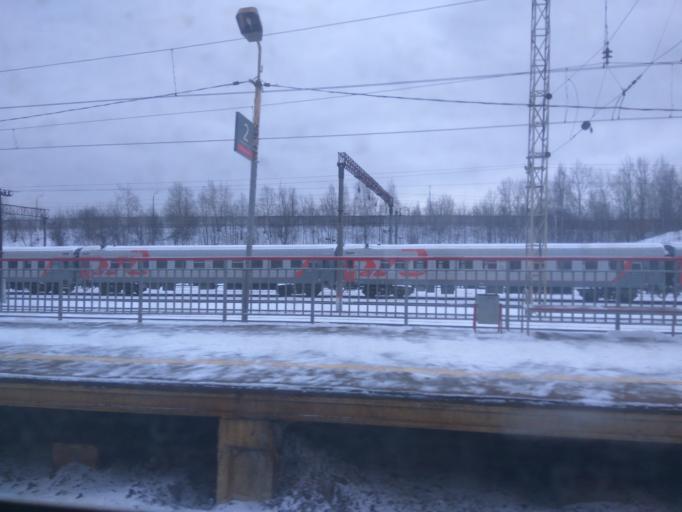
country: RU
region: Moscow
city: Annino
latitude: 55.5896
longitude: 37.6152
